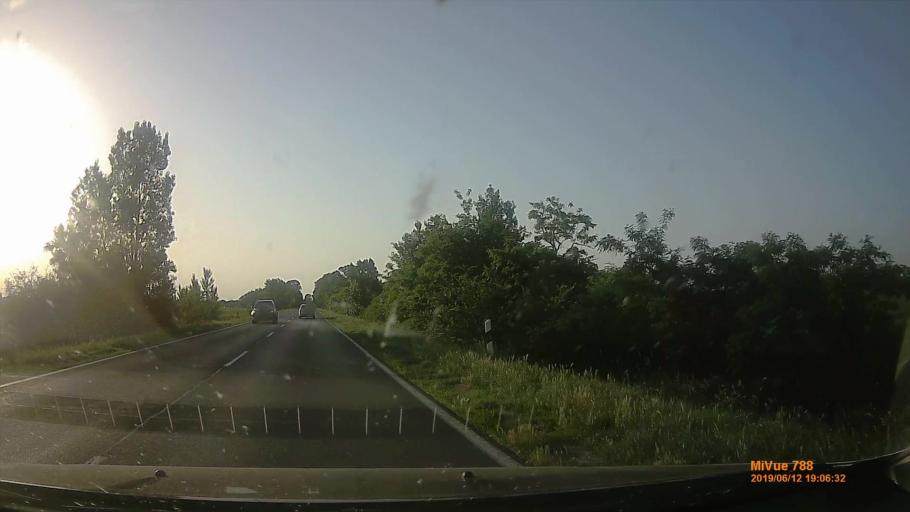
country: HU
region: Bacs-Kiskun
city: Varosfoeld
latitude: 46.7867
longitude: 19.7923
